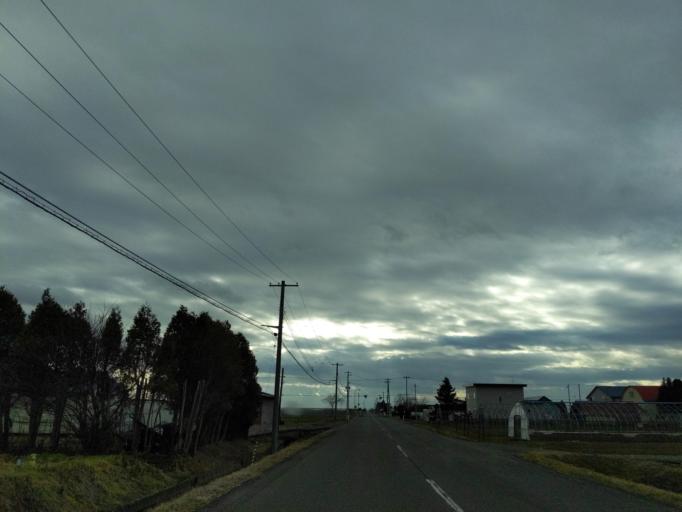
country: JP
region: Hokkaido
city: Kitahiroshima
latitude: 43.0320
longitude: 141.6845
